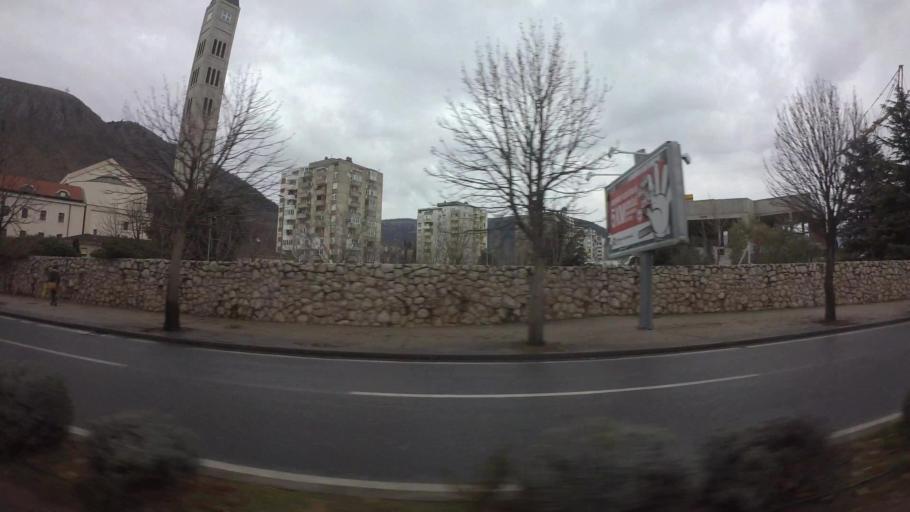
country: BA
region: Federation of Bosnia and Herzegovina
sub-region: Hercegovacko-Bosanski Kanton
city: Mostar
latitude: 43.3389
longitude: 17.8094
